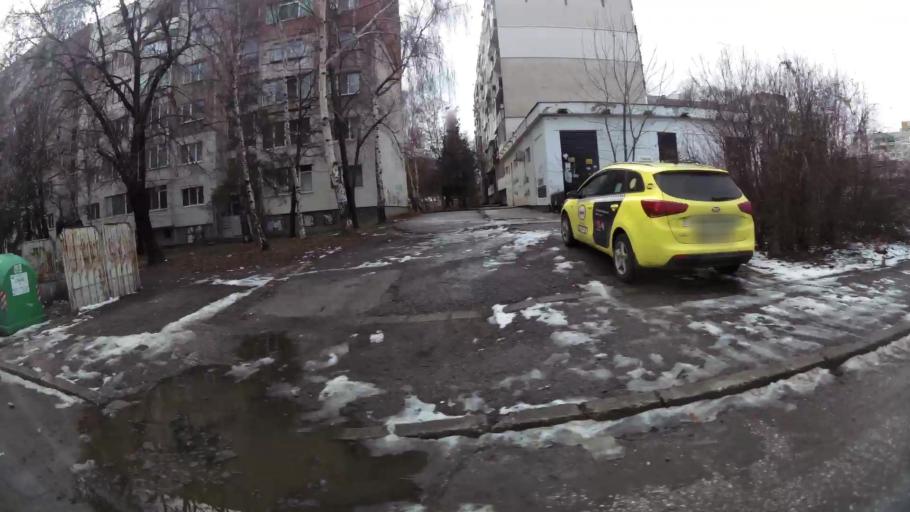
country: BG
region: Sofiya
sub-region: Obshtina Bozhurishte
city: Bozhurishte
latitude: 42.7160
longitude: 23.2471
